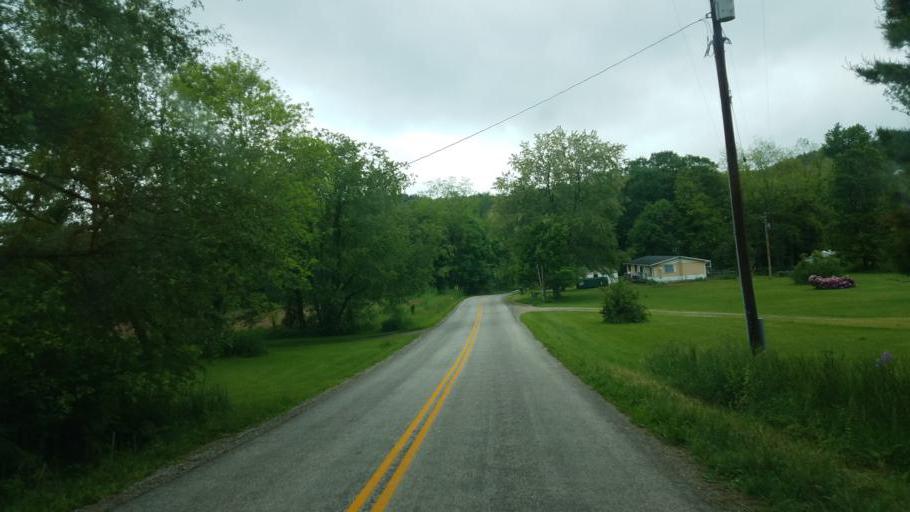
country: US
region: Ohio
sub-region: Ashland County
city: Ashland
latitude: 40.7607
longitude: -82.3445
